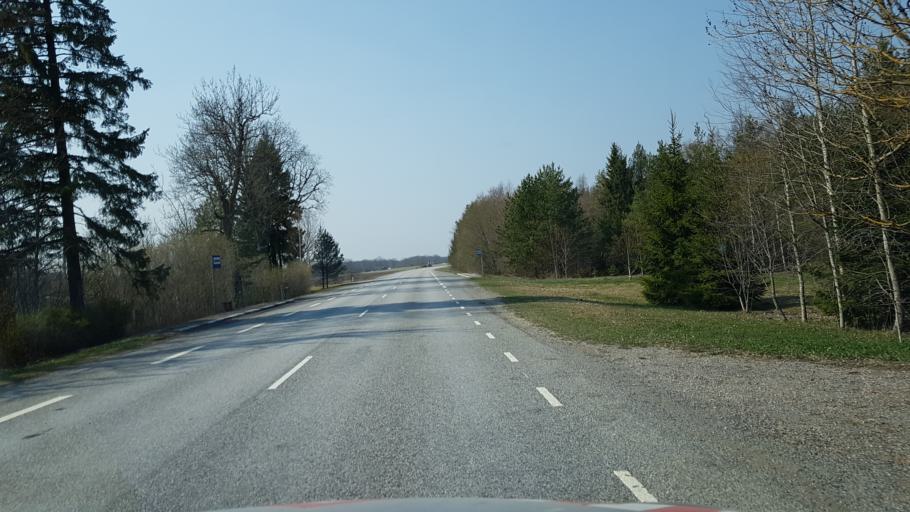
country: EE
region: Harju
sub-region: Paldiski linn
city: Paldiski
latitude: 59.2353
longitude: 23.9507
